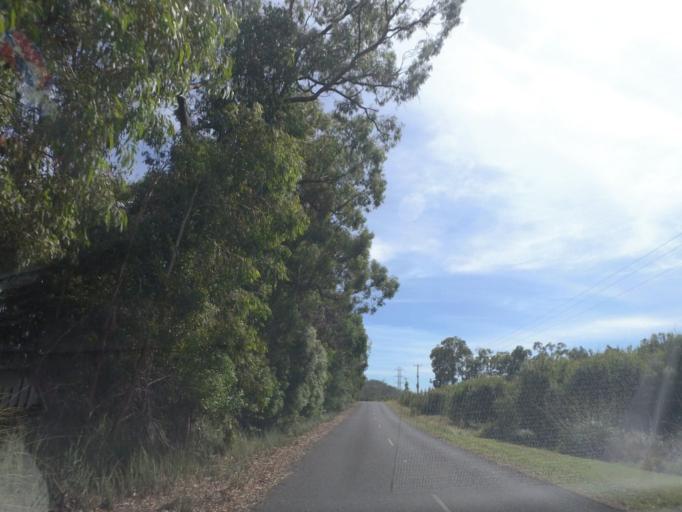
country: AU
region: Victoria
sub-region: Murrindindi
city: Kinglake West
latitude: -37.4642
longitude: 145.3980
